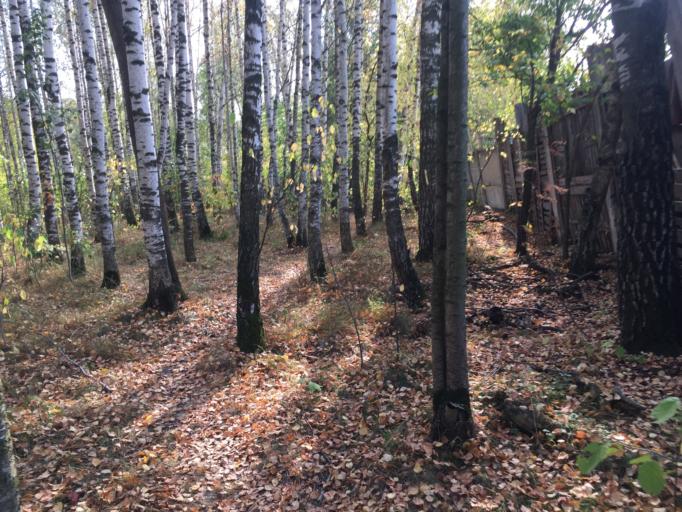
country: RU
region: Moscow
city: Babushkin
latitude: 55.8503
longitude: 37.7198
